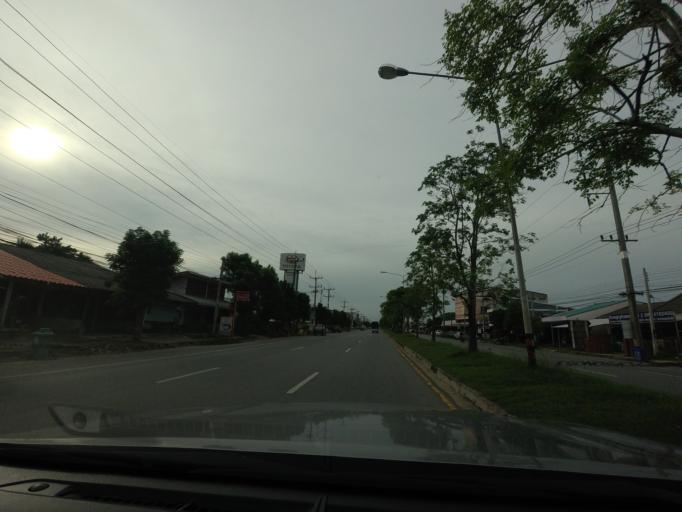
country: TH
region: Songkhla
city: Ranot
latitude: 7.7770
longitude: 100.3548
